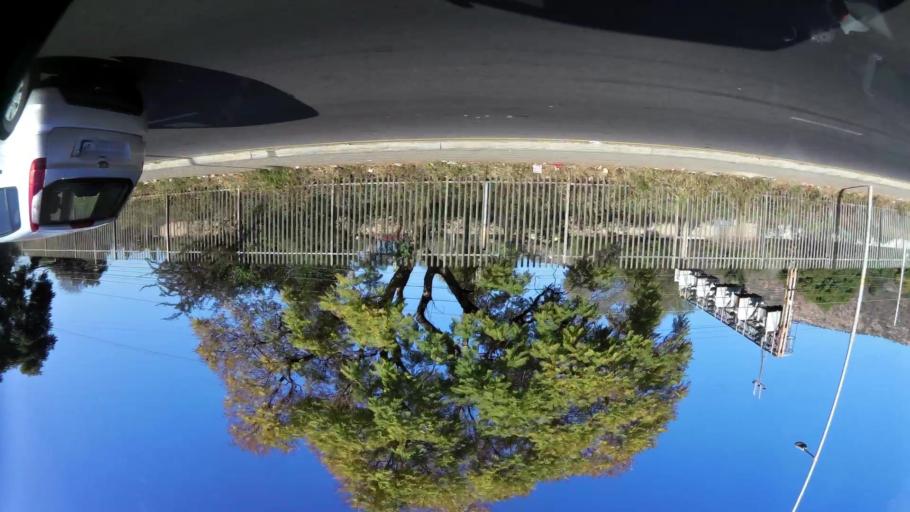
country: ZA
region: Gauteng
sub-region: City of Tshwane Metropolitan Municipality
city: Pretoria
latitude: -25.6841
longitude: 28.1834
